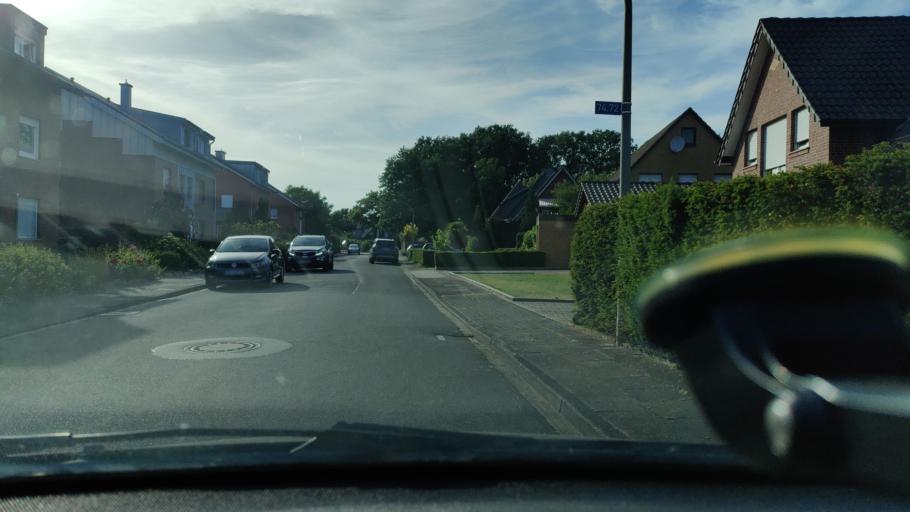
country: DE
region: North Rhine-Westphalia
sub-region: Regierungsbezirk Munster
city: Coesfeld
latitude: 51.9325
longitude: 7.1220
